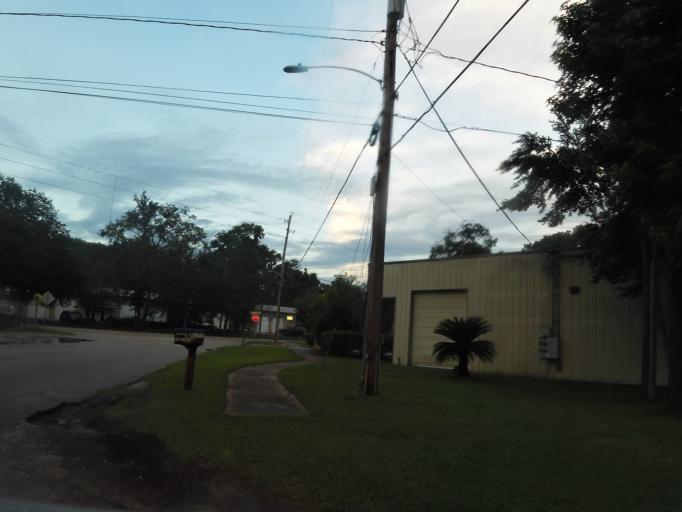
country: US
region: Florida
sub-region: Duval County
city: Jacksonville
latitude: 30.2747
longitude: -81.6411
